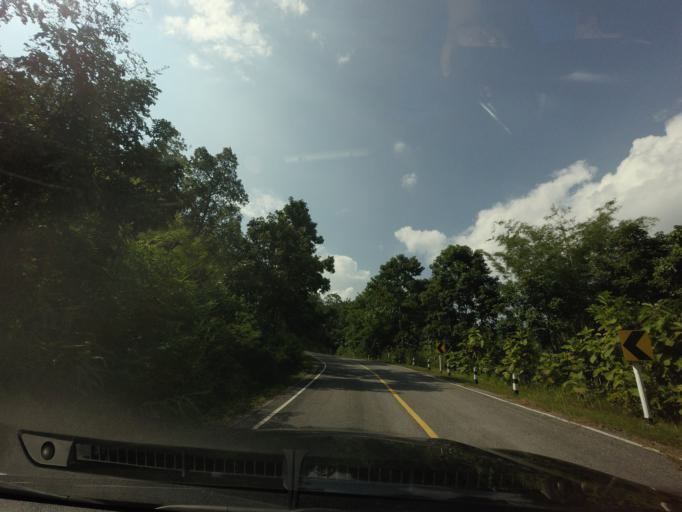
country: TH
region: Uttaradit
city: Ban Khok
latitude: 18.2381
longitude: 101.0082
